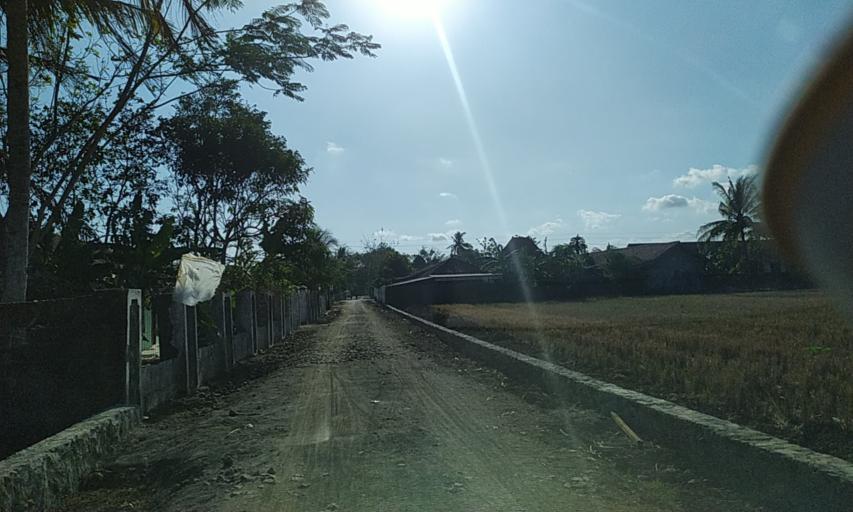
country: ID
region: Central Java
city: Kesugihan
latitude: -7.6231
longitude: 109.1310
